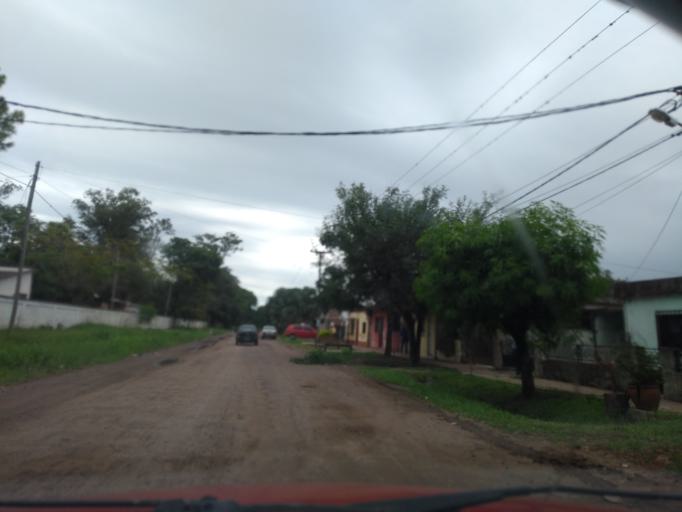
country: AR
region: Chaco
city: Barranqueras
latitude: -27.4773
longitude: -58.9586
